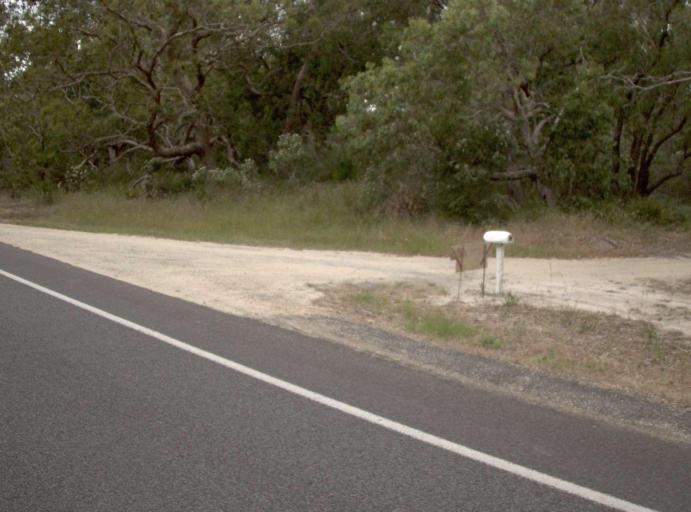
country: AU
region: Victoria
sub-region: Wellington
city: Sale
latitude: -38.1972
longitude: 147.0776
